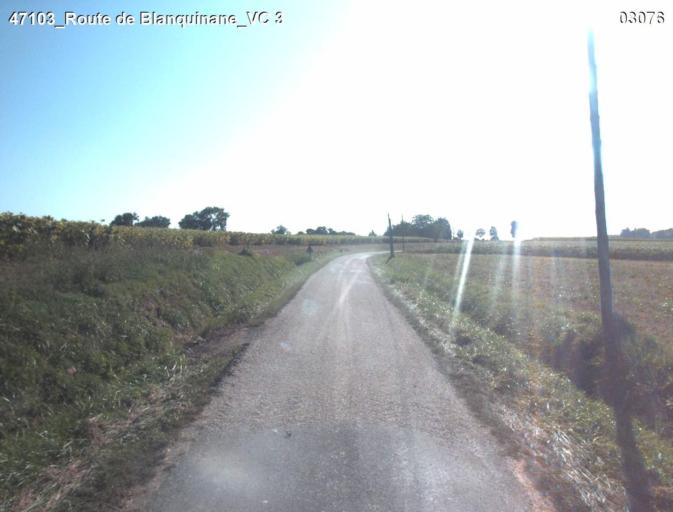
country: FR
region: Aquitaine
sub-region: Departement du Lot-et-Garonne
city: Nerac
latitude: 44.0900
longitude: 0.3295
